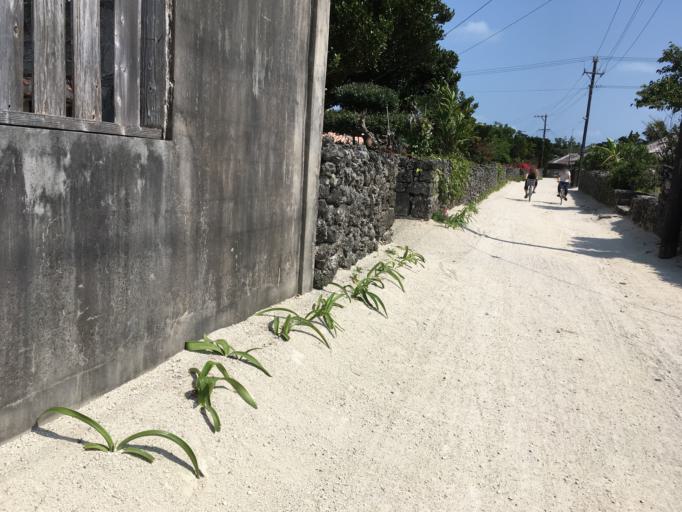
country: JP
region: Okinawa
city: Ishigaki
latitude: 24.3311
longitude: 124.0843
